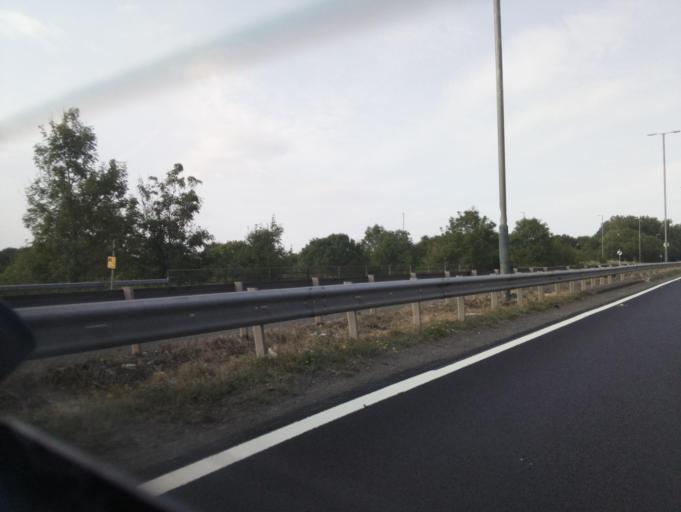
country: GB
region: England
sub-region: Warwickshire
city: Studley
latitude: 52.3091
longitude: -1.8732
